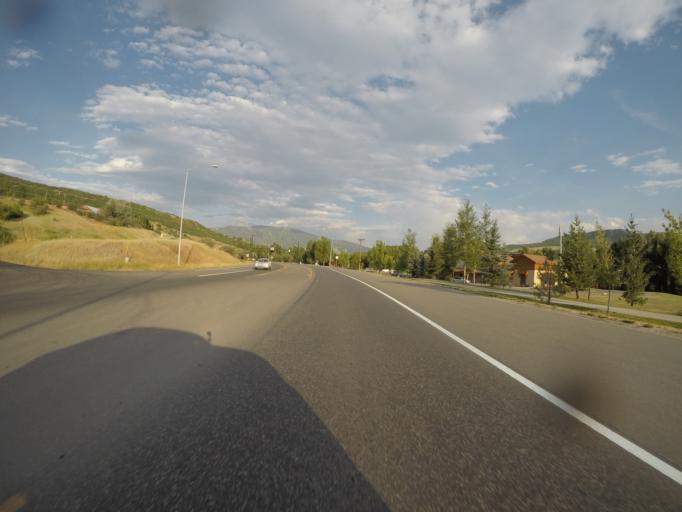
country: US
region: Colorado
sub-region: Routt County
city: Steamboat Springs
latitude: 40.4949
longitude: -106.8515
